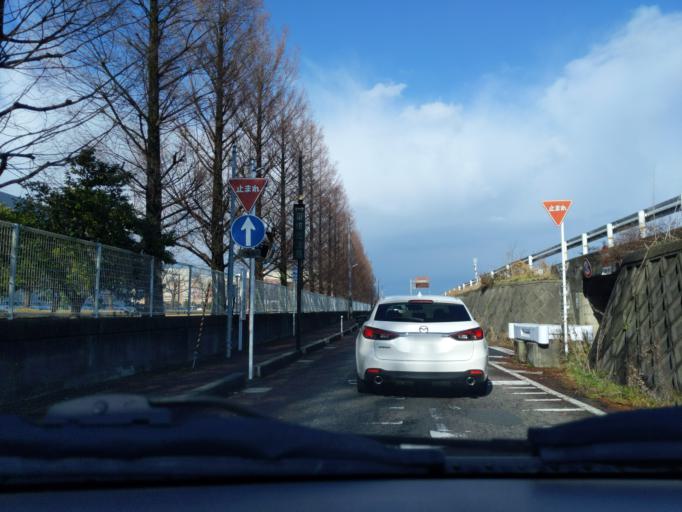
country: JP
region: Niigata
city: Kameda-honcho
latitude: 37.8745
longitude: 139.0850
